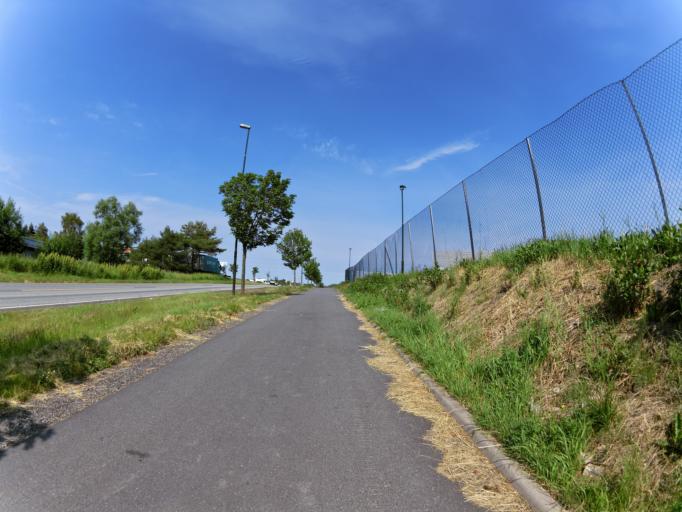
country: NO
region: Ostfold
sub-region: Sarpsborg
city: Sarpsborg
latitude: 59.2623
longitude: 11.1155
